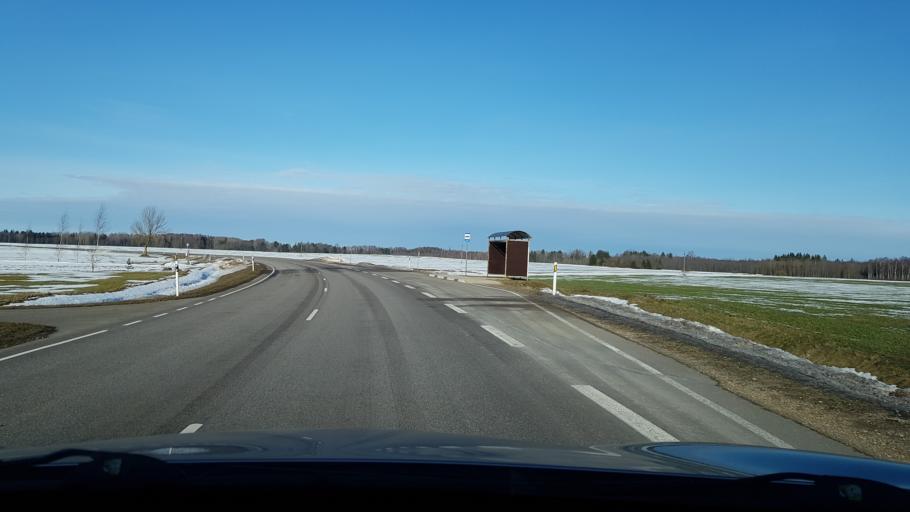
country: EE
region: Jogevamaa
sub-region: Poltsamaa linn
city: Poltsamaa
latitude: 58.6359
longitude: 25.7747
